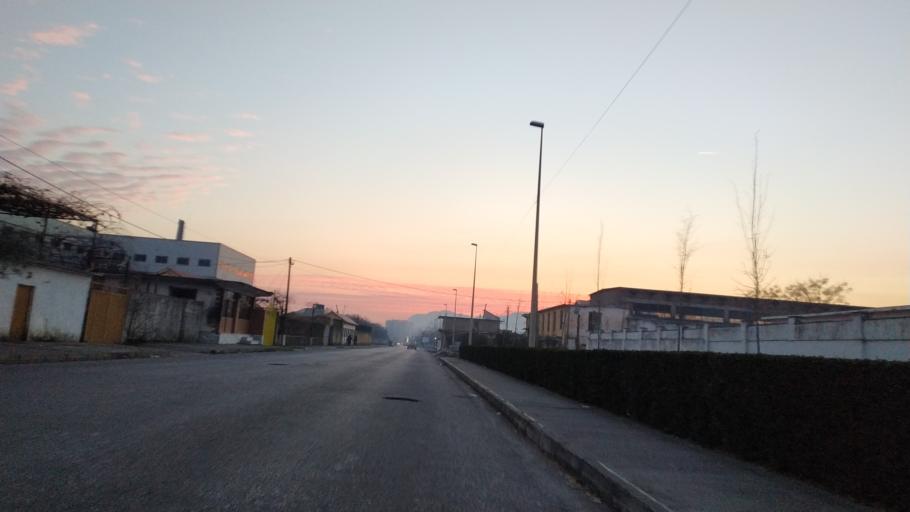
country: AL
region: Shkoder
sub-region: Rrethi i Shkodres
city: Shkoder
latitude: 42.0835
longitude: 19.5282
